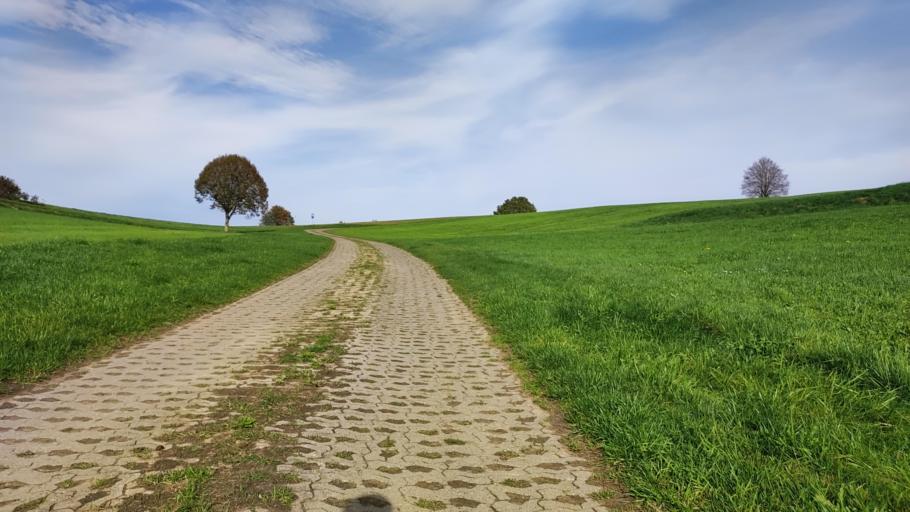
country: DE
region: Bavaria
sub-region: Swabia
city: Ziemetshausen
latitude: 48.2856
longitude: 10.5506
